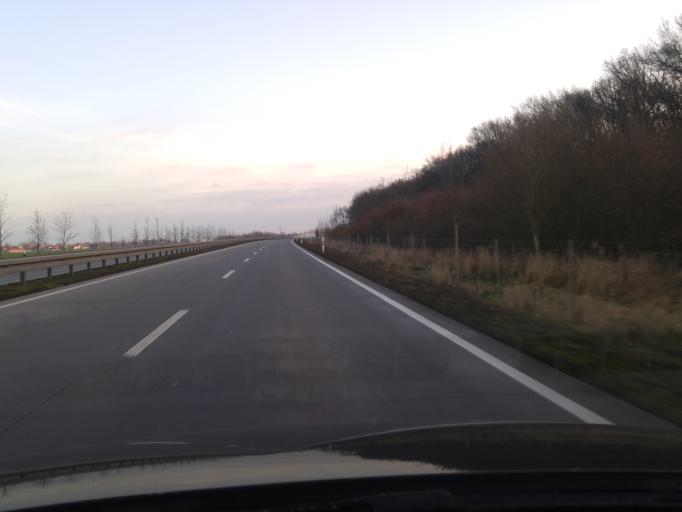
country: DE
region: Saxony
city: Rackwitz
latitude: 51.4075
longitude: 12.3233
